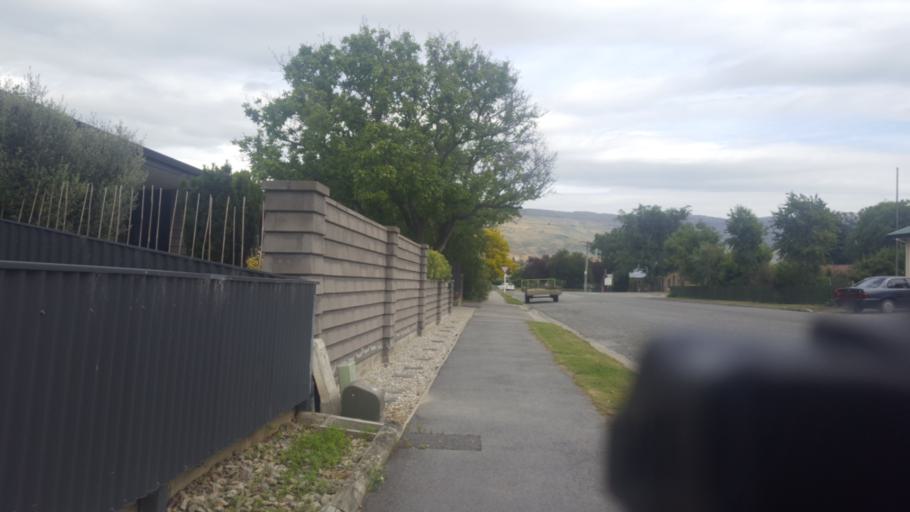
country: NZ
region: Otago
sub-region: Queenstown-Lakes District
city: Wanaka
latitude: -45.0483
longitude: 169.2107
